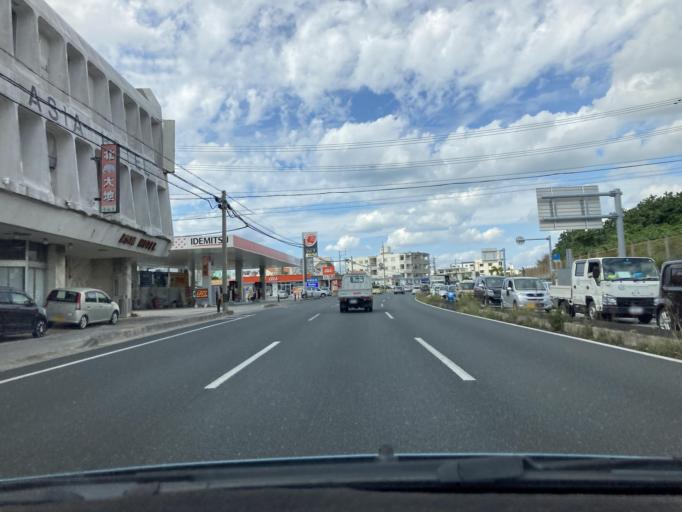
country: JP
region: Okinawa
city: Chatan
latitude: 26.3277
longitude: 127.7528
